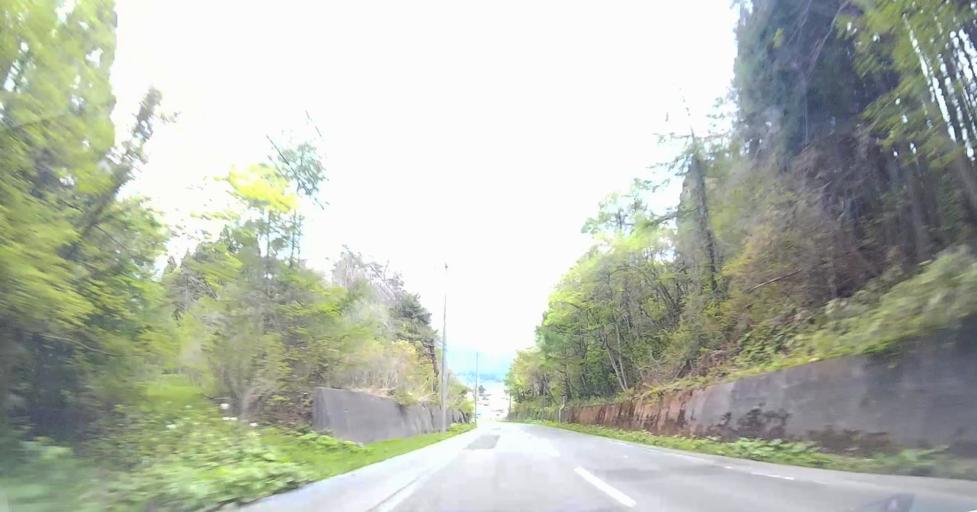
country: JP
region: Aomori
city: Goshogawara
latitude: 41.1766
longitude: 140.4881
